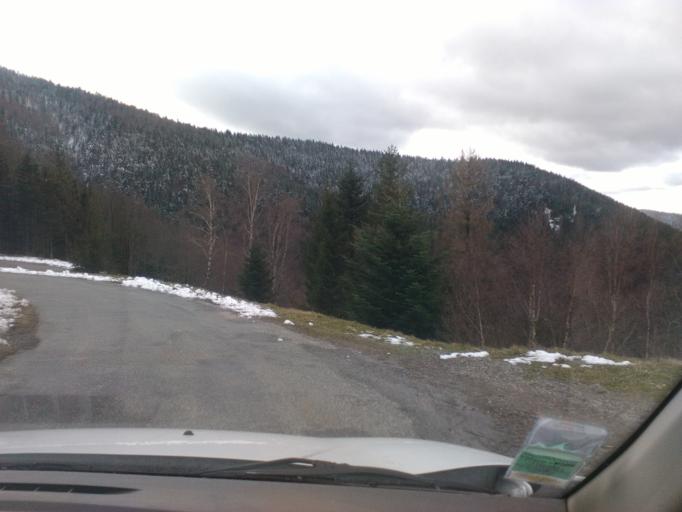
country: FR
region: Lorraine
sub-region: Departement des Vosges
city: Bussang
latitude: 47.8758
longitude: 6.8610
